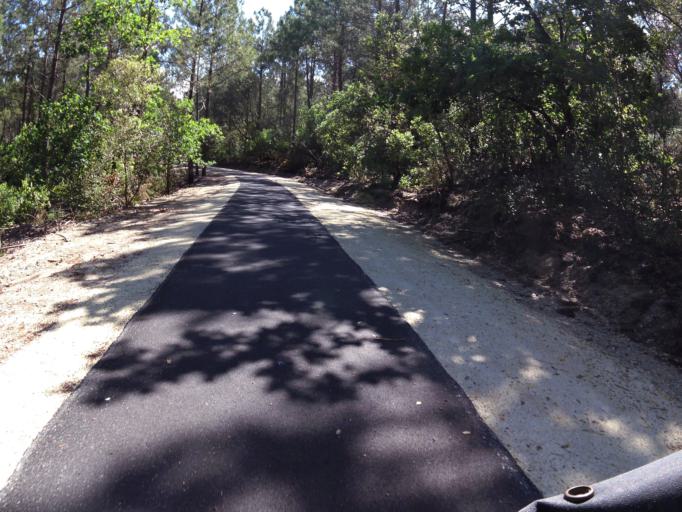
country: FR
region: Aquitaine
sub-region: Departement de la Gironde
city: Lacanau
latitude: 45.0296
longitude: -1.1593
